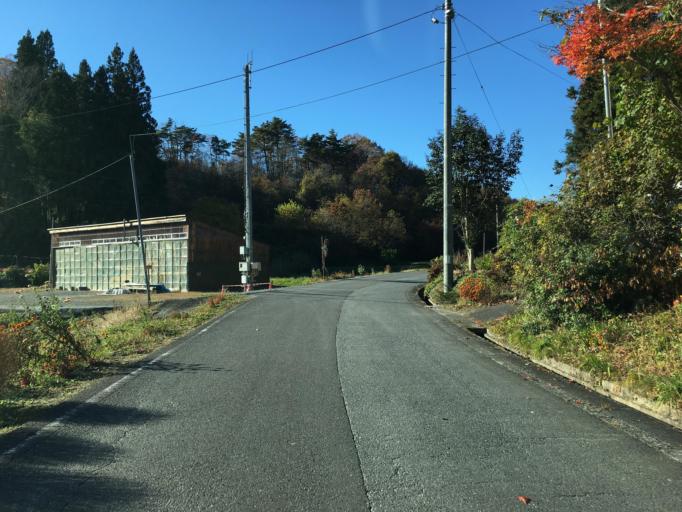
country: JP
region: Fukushima
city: Ishikawa
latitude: 37.2241
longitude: 140.5228
